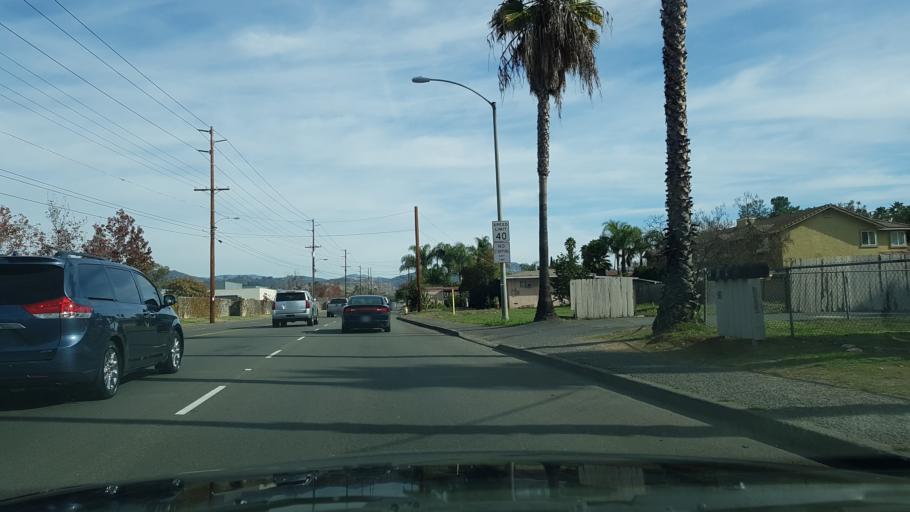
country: US
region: California
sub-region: San Diego County
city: Escondido
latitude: 33.1364
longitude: -117.0783
